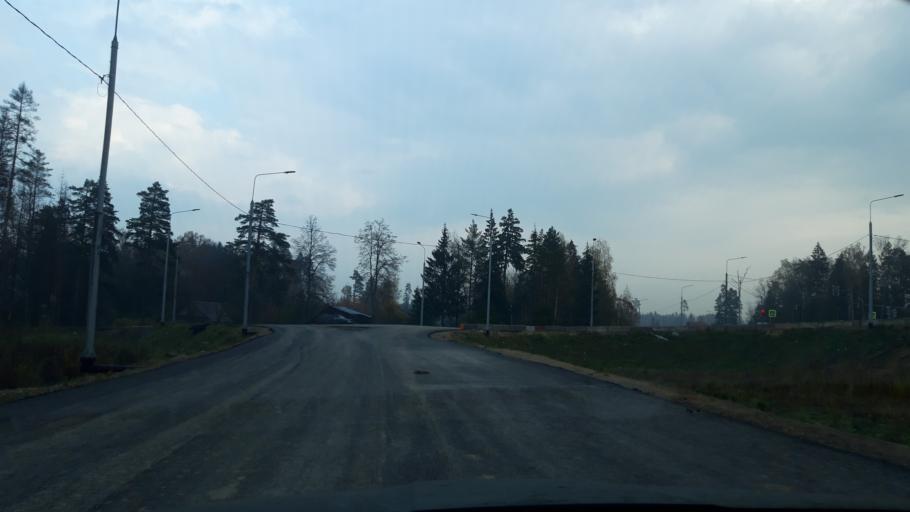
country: RU
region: Moskovskaya
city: Lozhki
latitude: 56.0448
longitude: 37.1039
